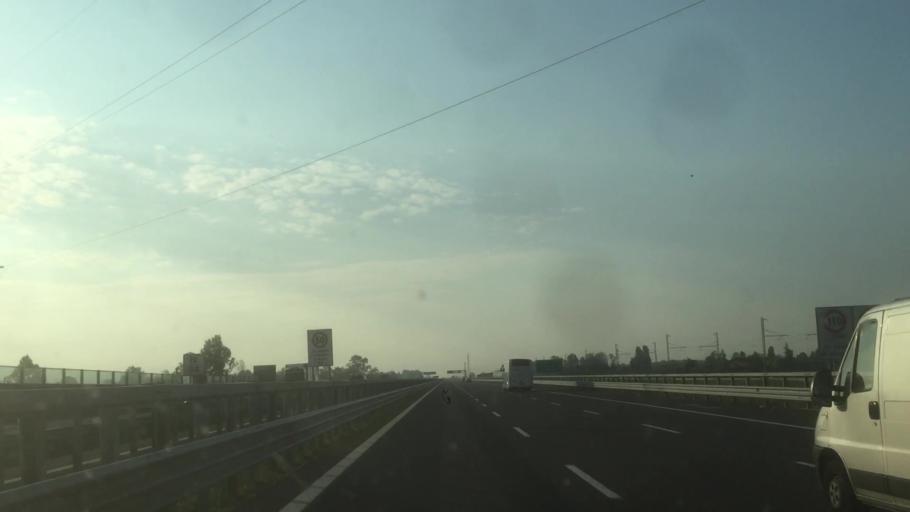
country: IT
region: Lombardy
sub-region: Provincia di Bergamo
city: Bariano
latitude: 45.5048
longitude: 9.7016
